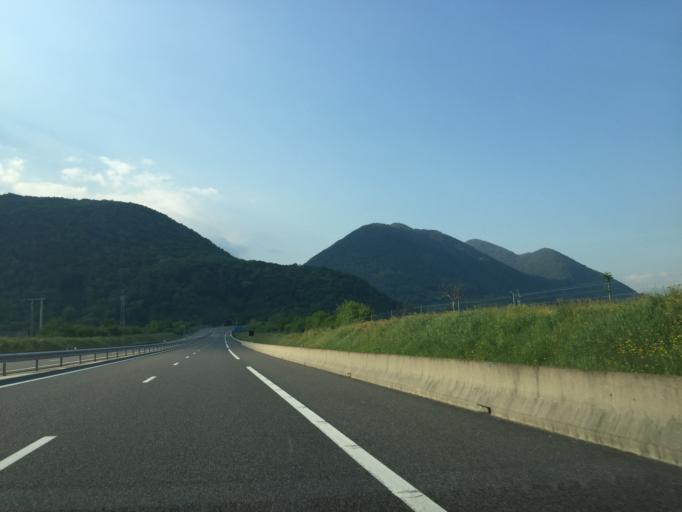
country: FR
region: Rhone-Alpes
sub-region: Departement de l'Isere
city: Vif
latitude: 45.0609
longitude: 5.6839
